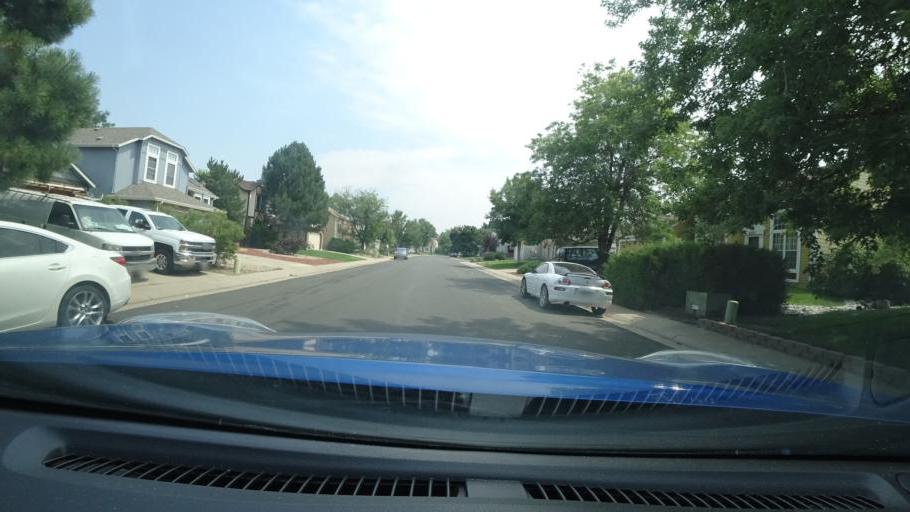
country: US
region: Colorado
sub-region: Adams County
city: Aurora
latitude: 39.7771
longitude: -104.7471
